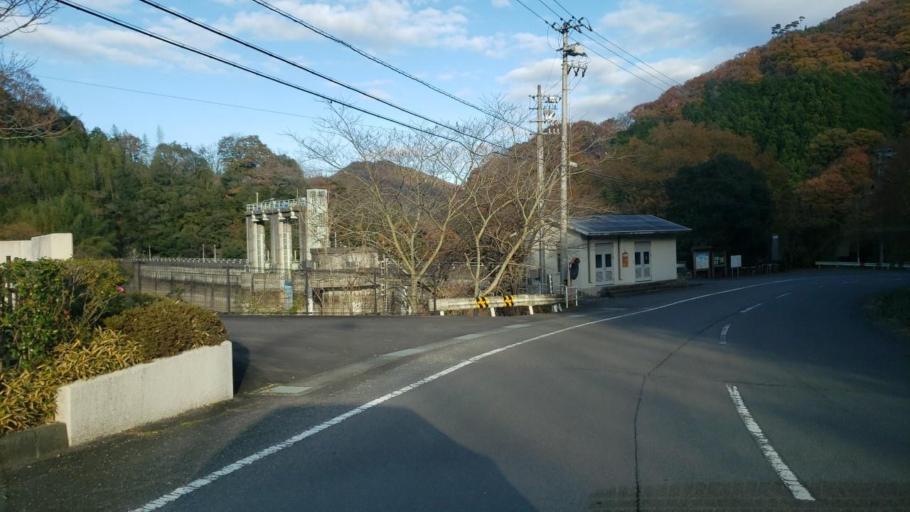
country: JP
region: Tokushima
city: Wakimachi
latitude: 34.1681
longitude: 134.0736
